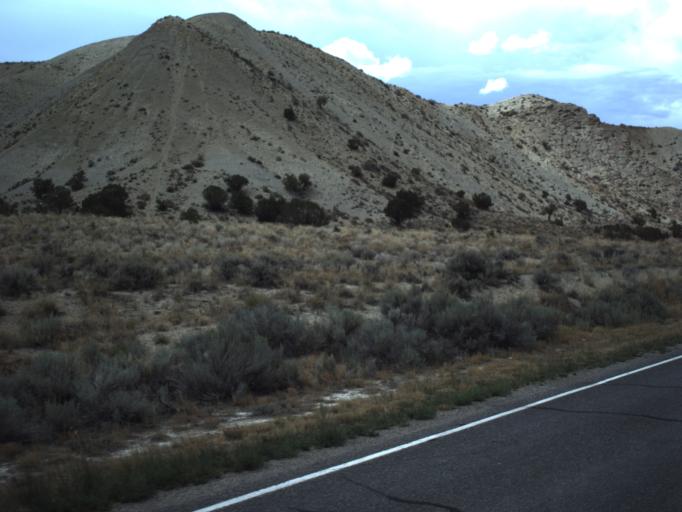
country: US
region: Utah
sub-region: Sanpete County
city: Centerfield
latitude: 39.1360
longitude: -111.7299
